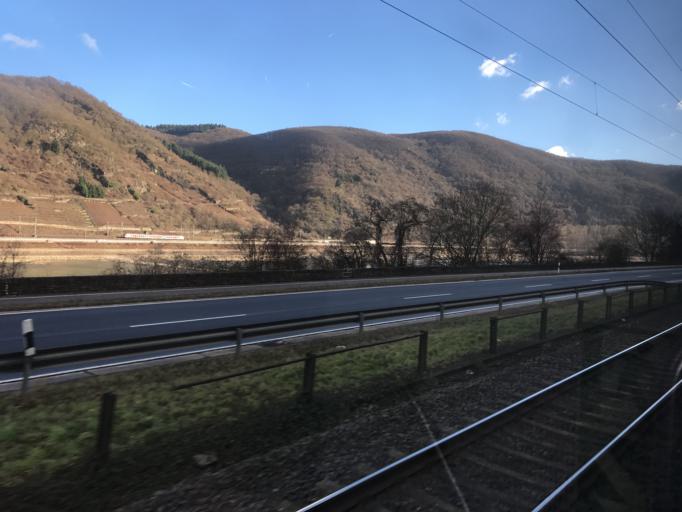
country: DE
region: Rheinland-Pfalz
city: Kaub
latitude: 50.0794
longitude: 7.7656
